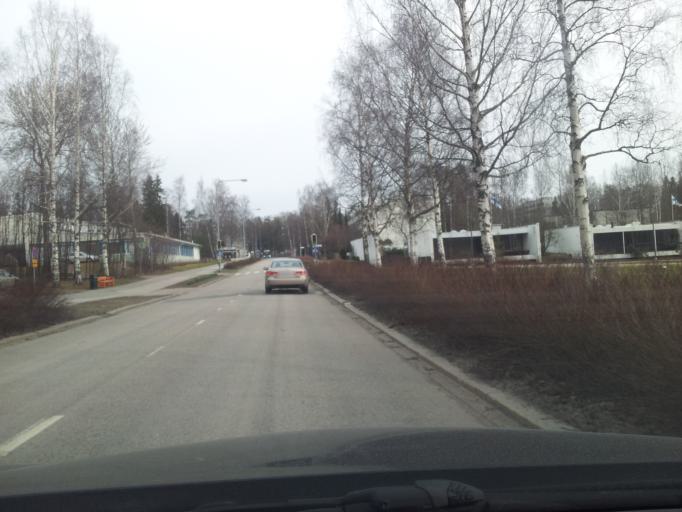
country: FI
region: Uusimaa
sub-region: Helsinki
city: Otaniemi
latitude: 60.1854
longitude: 24.7961
